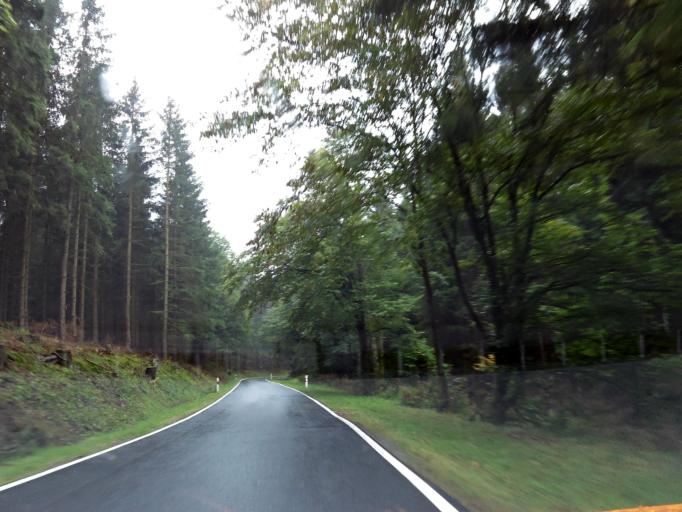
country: DE
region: Saxony-Anhalt
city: Hasselfelde
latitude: 51.6498
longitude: 10.8350
